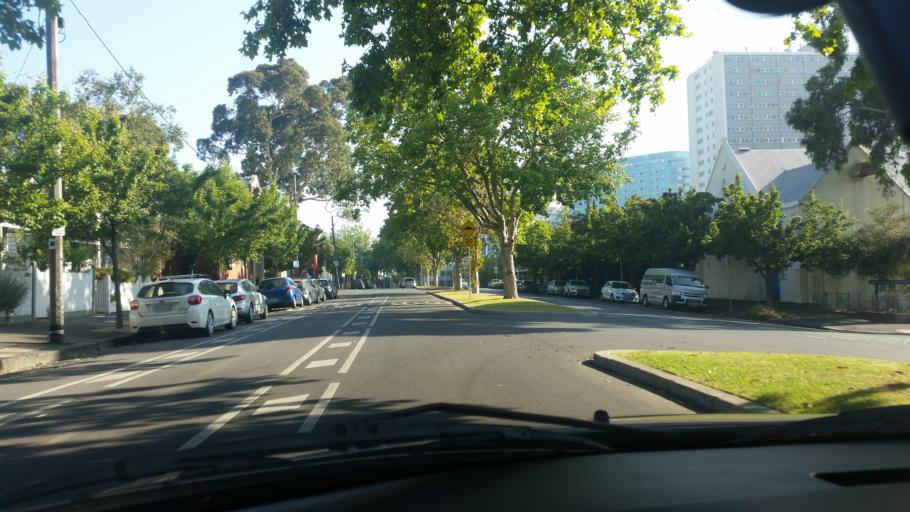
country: AU
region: Victoria
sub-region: Melbourne
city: North Melbourne
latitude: -37.7939
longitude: 144.9420
